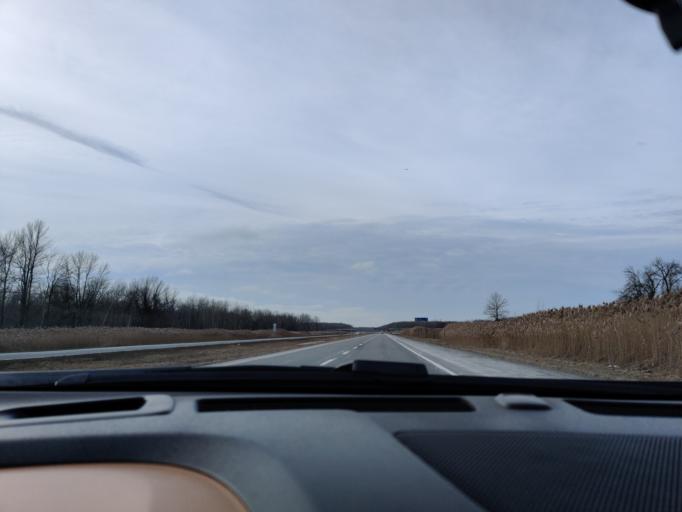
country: CA
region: Quebec
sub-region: Monteregie
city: Les Coteaux
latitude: 45.2392
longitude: -74.2805
